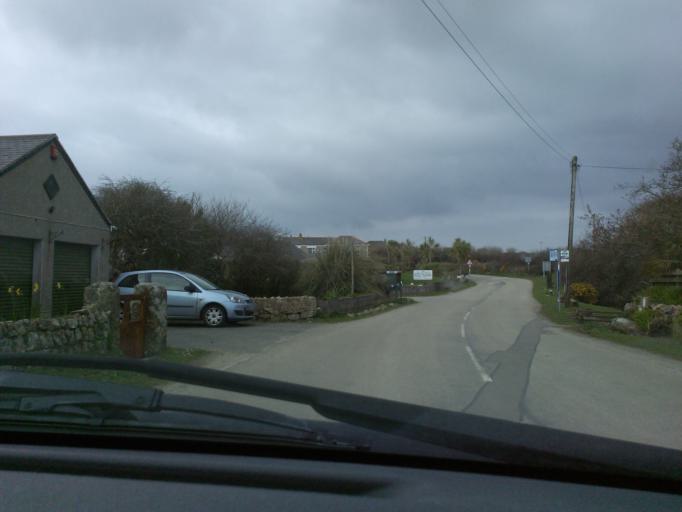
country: GB
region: England
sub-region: Cornwall
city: Sennen
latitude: 50.0561
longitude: -5.6667
